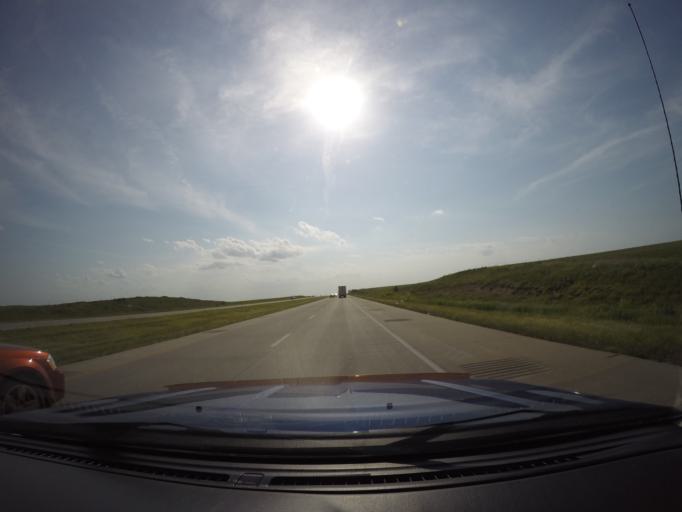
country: US
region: Kansas
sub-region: Wabaunsee County
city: Alma
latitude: 39.0654
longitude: -96.4217
